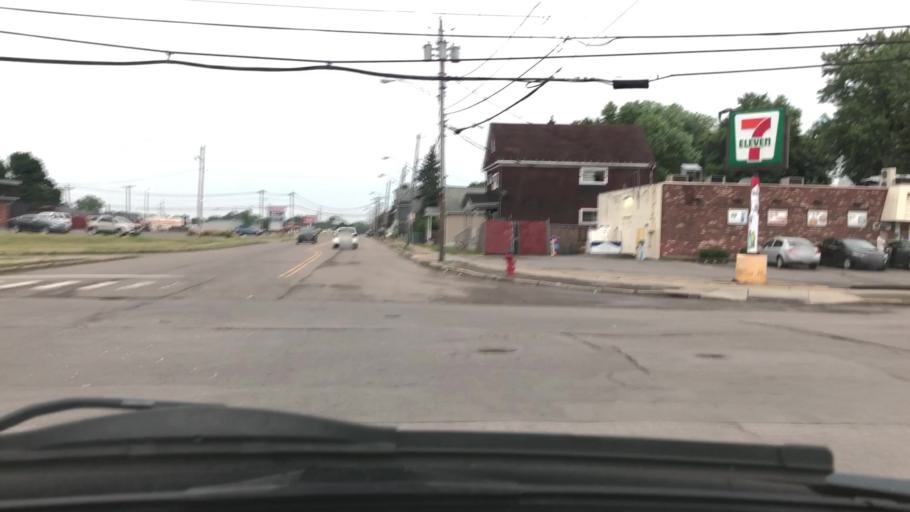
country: US
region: New York
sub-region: Erie County
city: Sloan
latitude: 42.8777
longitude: -78.8012
